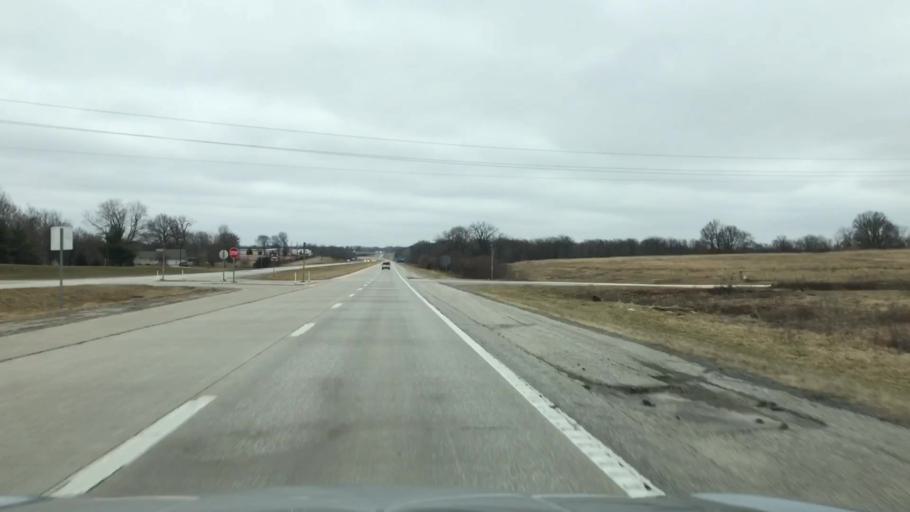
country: US
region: Missouri
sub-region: Linn County
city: Brookfield
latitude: 39.7786
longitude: -93.0997
